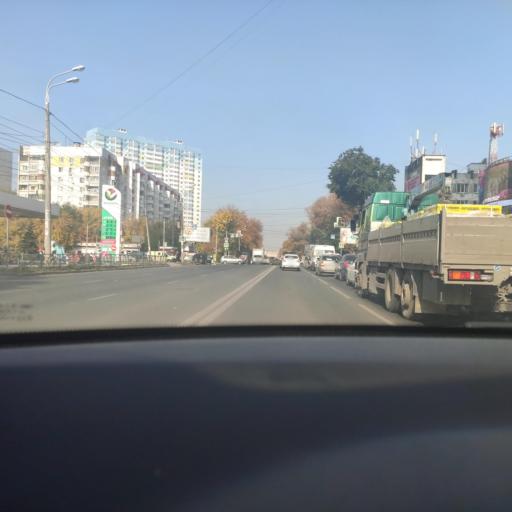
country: RU
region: Samara
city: Samara
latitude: 53.2049
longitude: 50.1898
